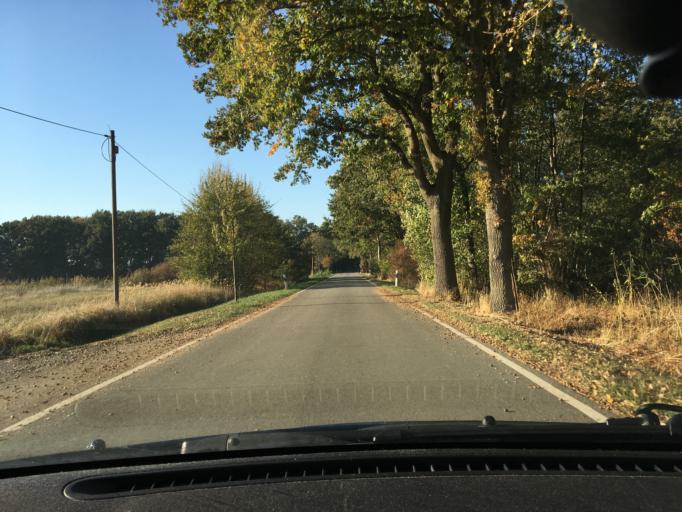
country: DE
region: Lower Saxony
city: Hitzacker
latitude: 53.1939
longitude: 11.0016
